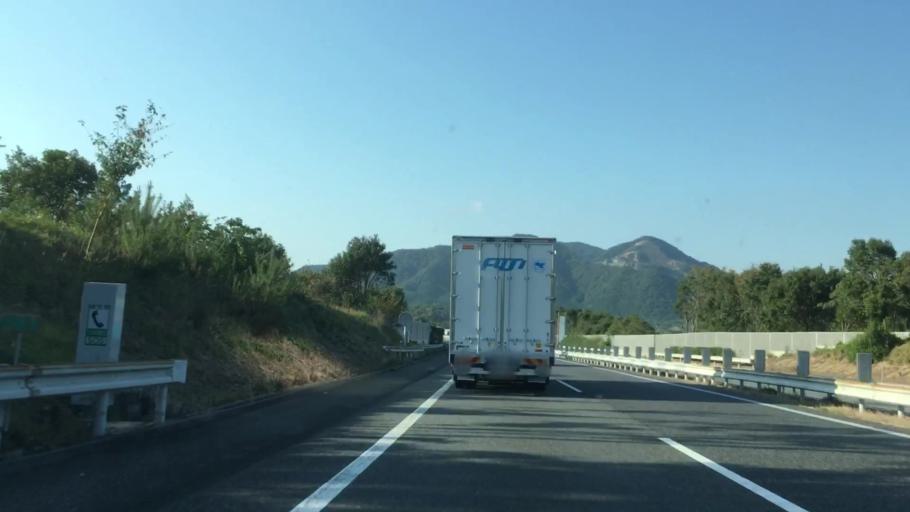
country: JP
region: Yamaguchi
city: Hofu
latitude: 34.0672
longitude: 131.5001
